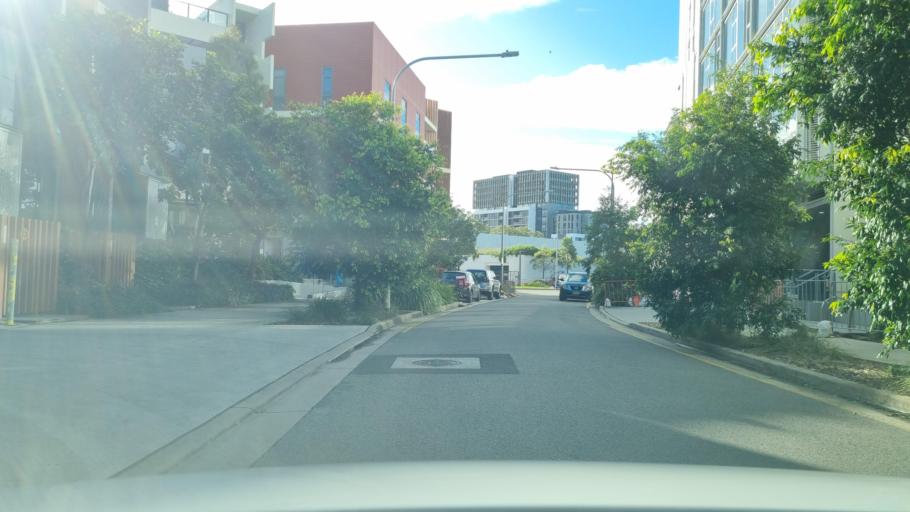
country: AU
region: New South Wales
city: Alexandria
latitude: -33.9103
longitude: 151.2080
